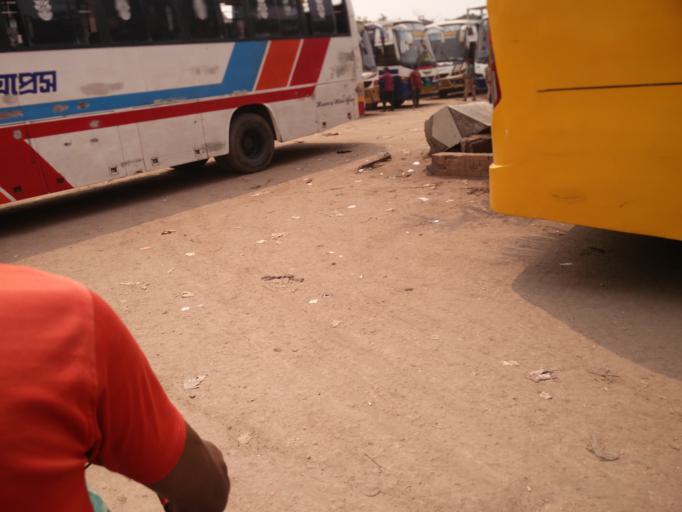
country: BD
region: Dhaka
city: Mymensingh
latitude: 24.7351
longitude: 90.4084
